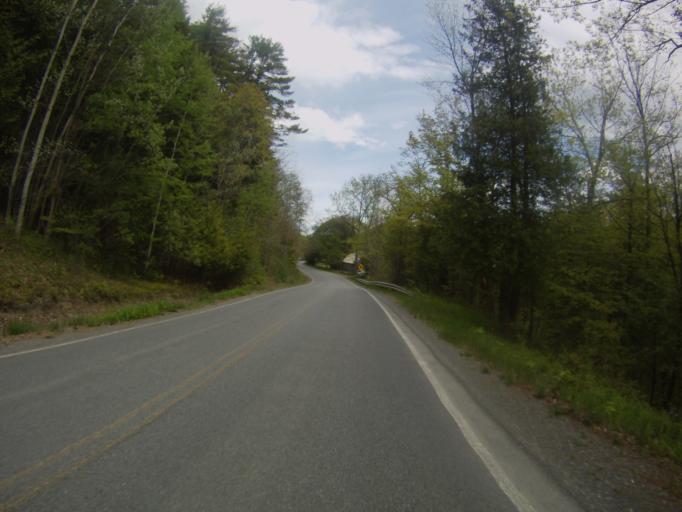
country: US
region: New York
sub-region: Essex County
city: Ticonderoga
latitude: 43.9415
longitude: -73.4721
